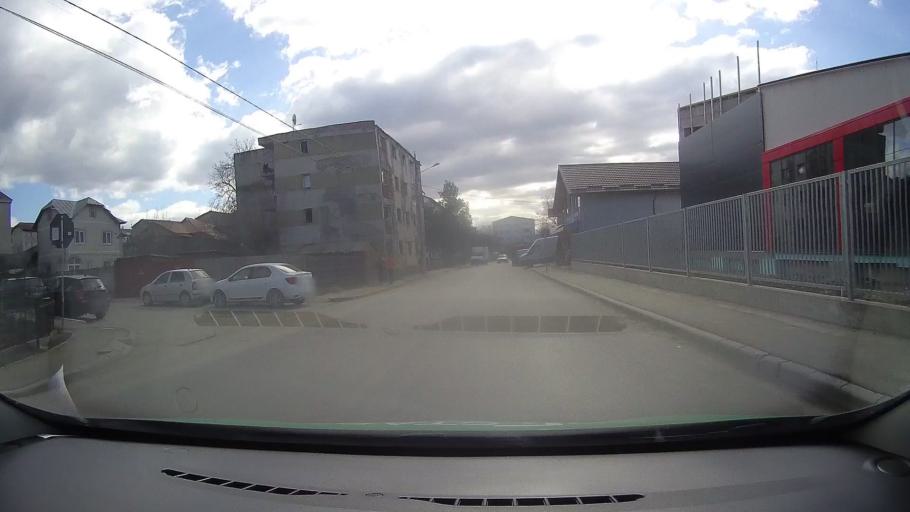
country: RO
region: Dambovita
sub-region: Oras Pucioasa
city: Pucioasa
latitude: 45.0728
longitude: 25.4327
